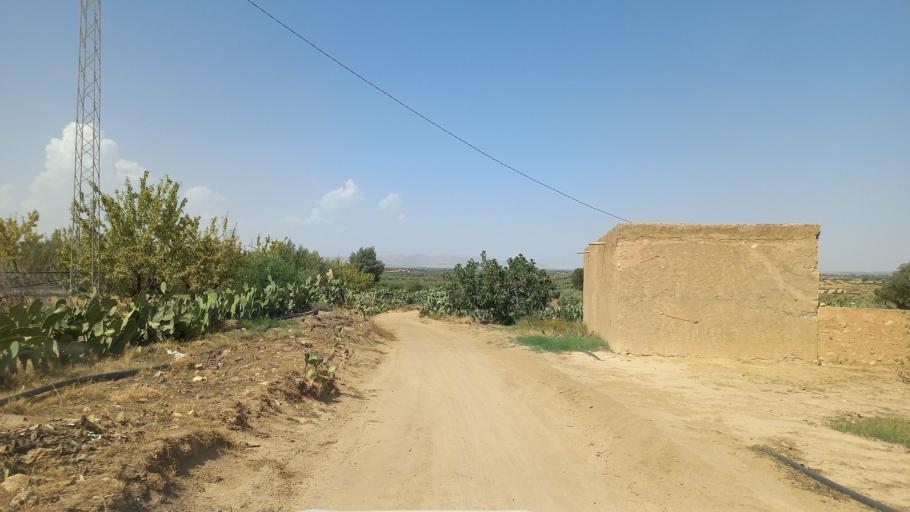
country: TN
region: Al Qasrayn
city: Kasserine
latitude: 35.2189
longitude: 9.0432
